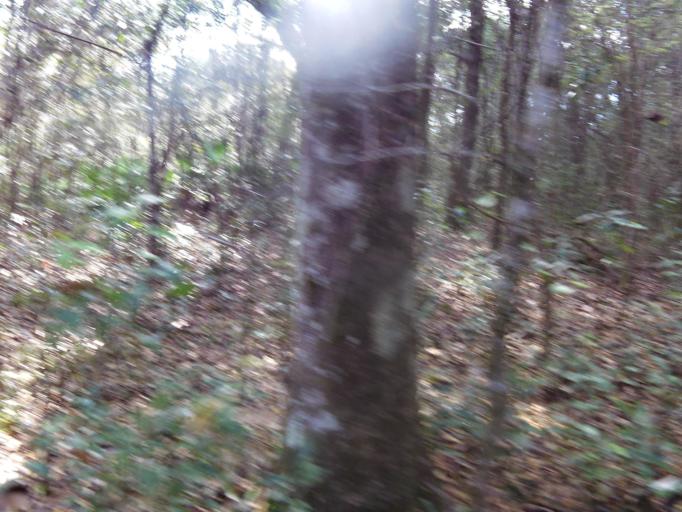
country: US
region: Florida
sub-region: Putnam County
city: Interlachen
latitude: 29.7640
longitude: -81.8275
